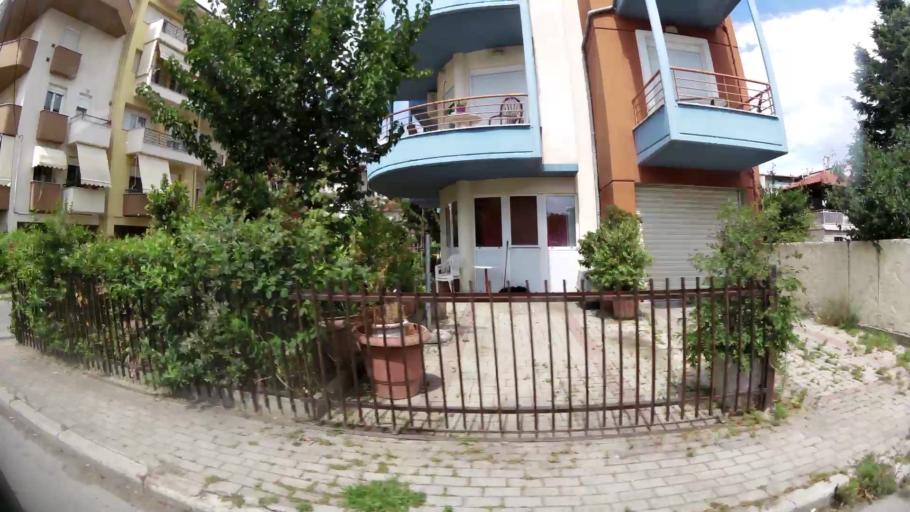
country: GR
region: Central Macedonia
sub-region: Nomos Pierias
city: Katerini
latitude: 40.2755
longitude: 22.4994
